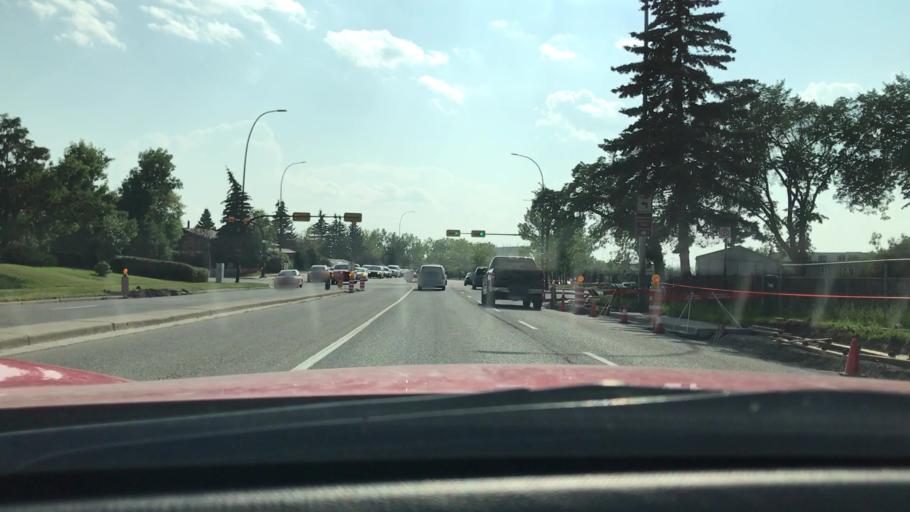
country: CA
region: Alberta
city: Calgary
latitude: 51.0192
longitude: -114.1519
